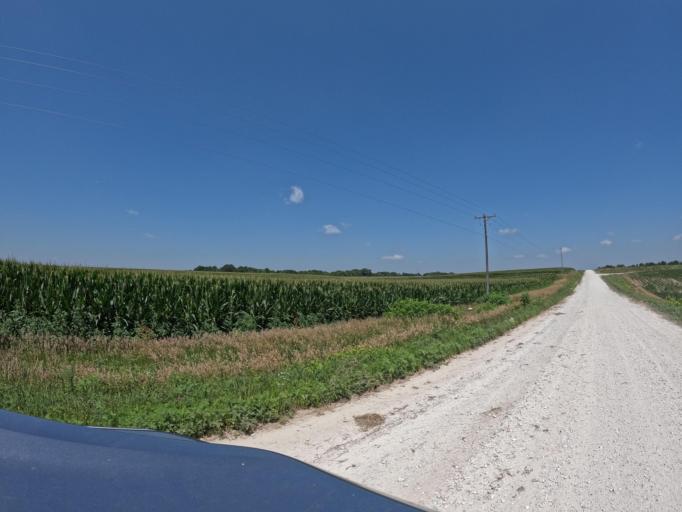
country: US
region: Iowa
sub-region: Keokuk County
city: Sigourney
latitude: 41.2781
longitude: -92.2381
